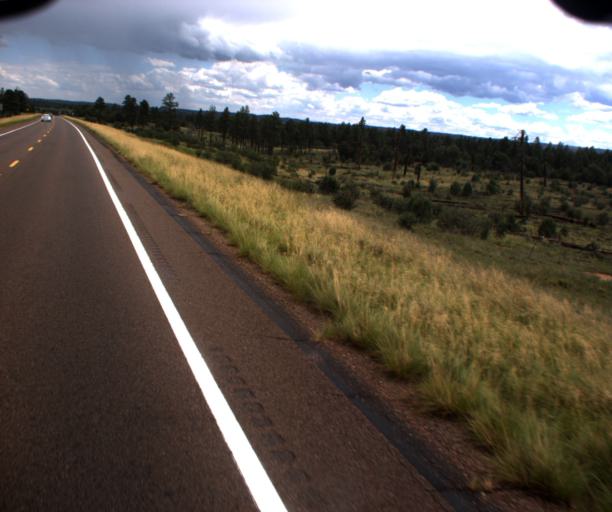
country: US
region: Arizona
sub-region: Navajo County
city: Linden
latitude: 34.3643
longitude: -110.3451
